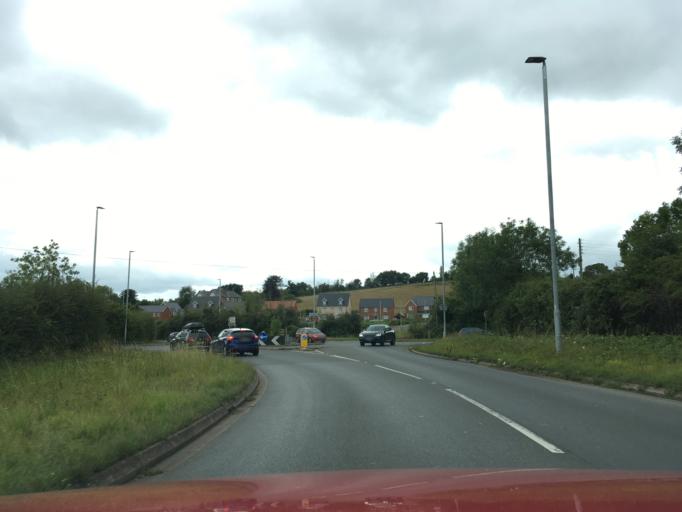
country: GB
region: England
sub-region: Devon
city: Exminster
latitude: 50.6753
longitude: -3.4864
